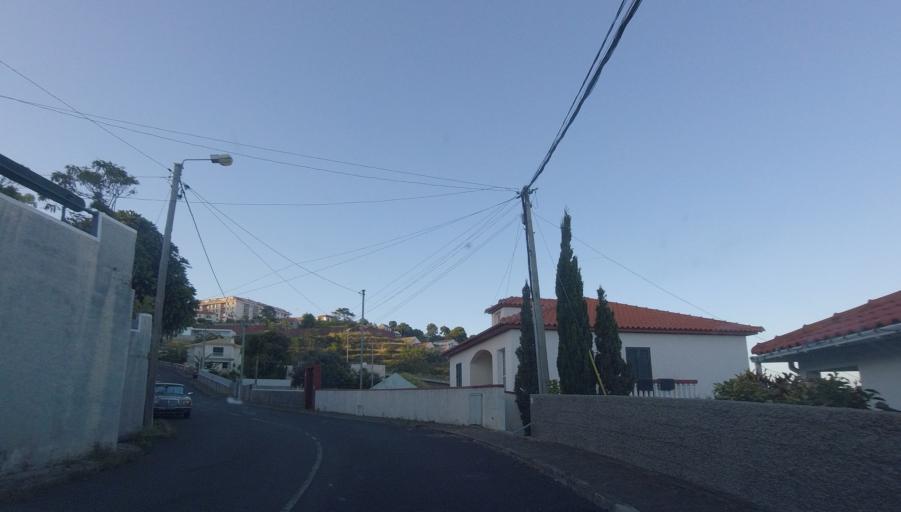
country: PT
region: Madeira
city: Canico
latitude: 32.6470
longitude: -16.8398
